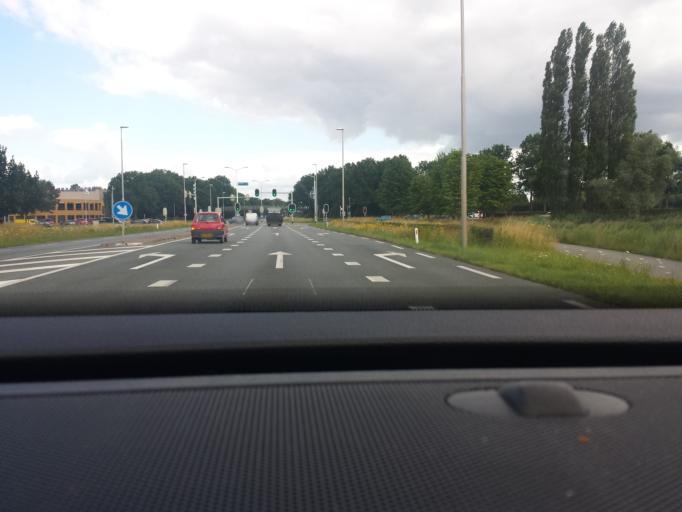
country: NL
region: Gelderland
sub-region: Gemeente Zutphen
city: Warnsveld
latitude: 52.1366
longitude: 6.2189
